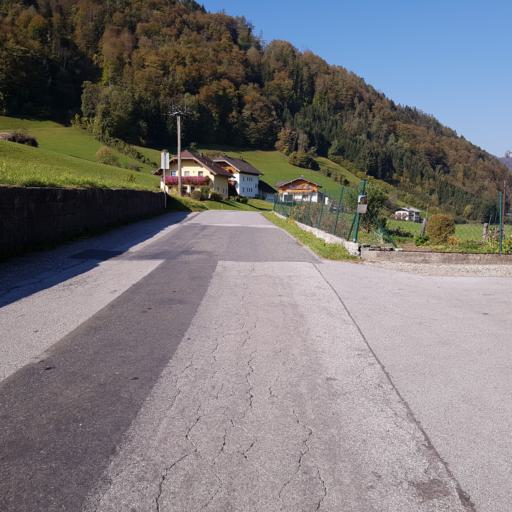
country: AT
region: Salzburg
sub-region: Politischer Bezirk Hallein
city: Hallein
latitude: 47.6640
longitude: 13.1141
